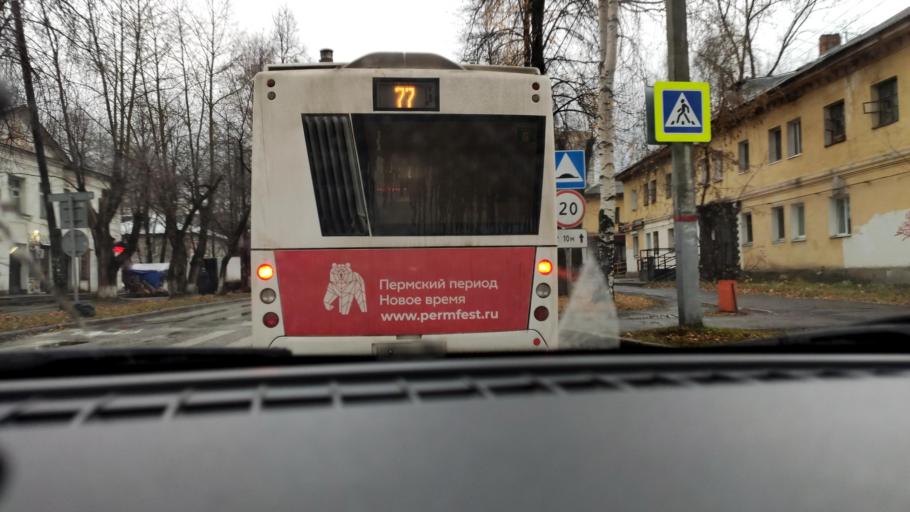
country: RU
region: Perm
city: Perm
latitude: 58.1094
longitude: 56.3767
